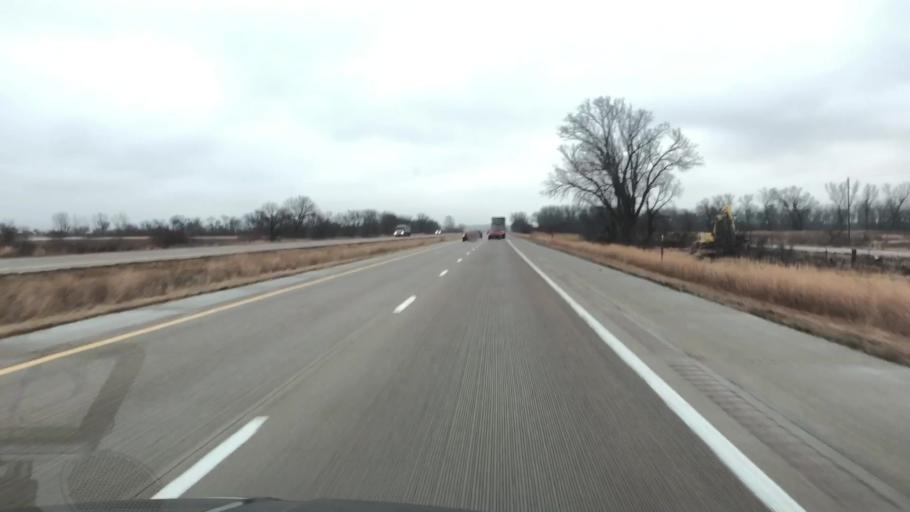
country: US
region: Nebraska
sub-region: Burt County
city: Tekamah
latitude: 41.8460
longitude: -96.0947
